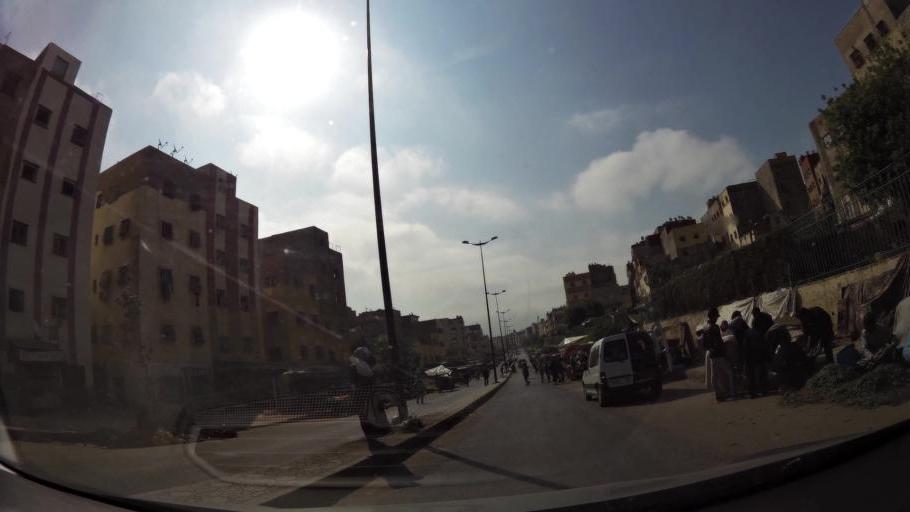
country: MA
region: Fes-Boulemane
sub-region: Fes
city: Fes
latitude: 34.0696
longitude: -5.0100
